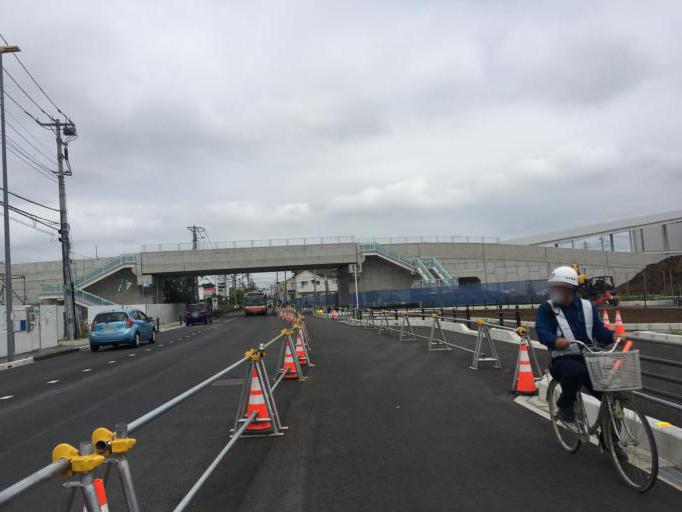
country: JP
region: Saitama
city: Ageoshimo
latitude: 35.9640
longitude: 139.5983
